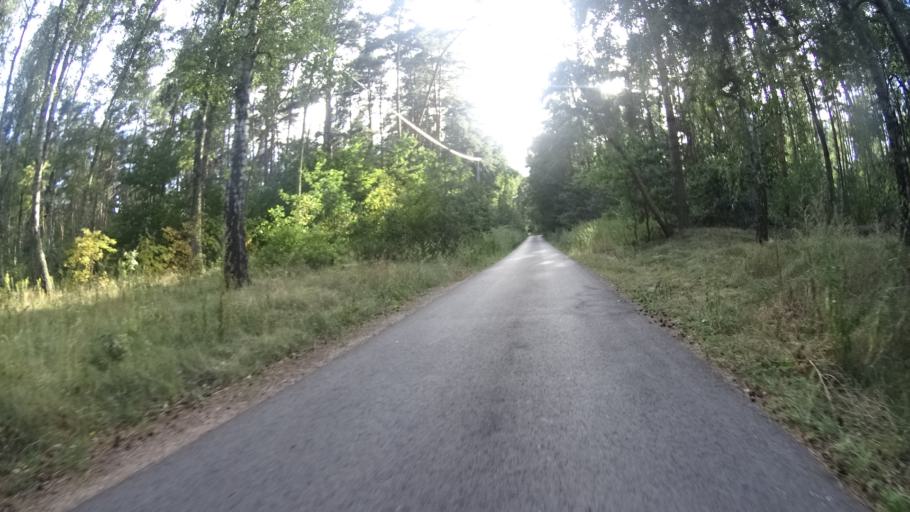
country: PL
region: Masovian Voivodeship
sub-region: Powiat bialobrzeski
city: Wysmierzyce
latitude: 51.6755
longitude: 20.8081
